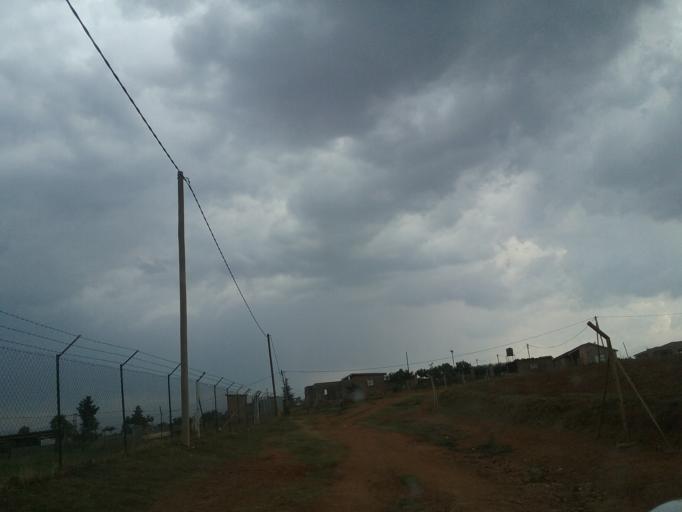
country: LS
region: Maseru
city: Maseru
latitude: -29.4191
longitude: 27.5678
